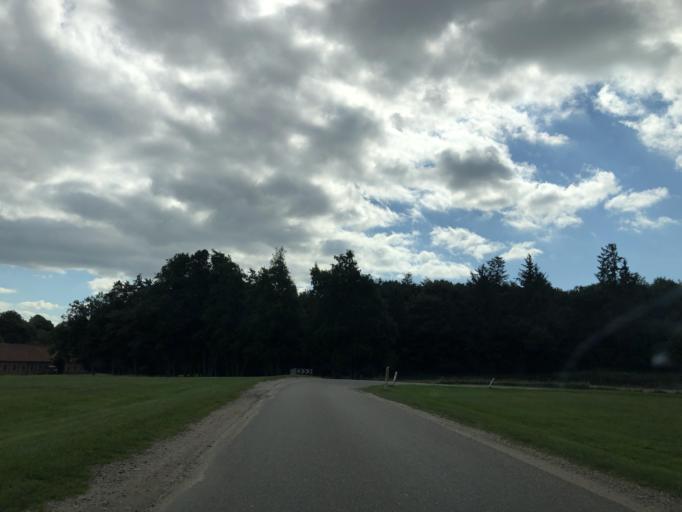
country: DK
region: Central Jutland
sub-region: Viborg Kommune
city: Viborg
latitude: 56.5663
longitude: 9.3225
